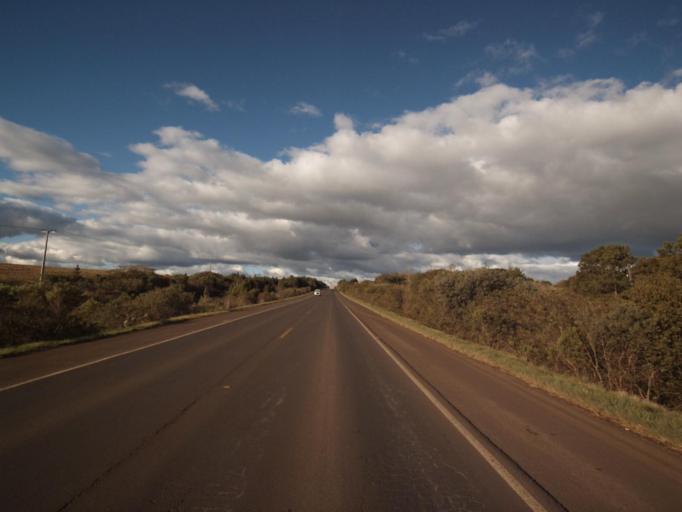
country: BR
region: Santa Catarina
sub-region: Campos Novos
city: Campos Novos
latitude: -27.3604
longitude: -51.2981
